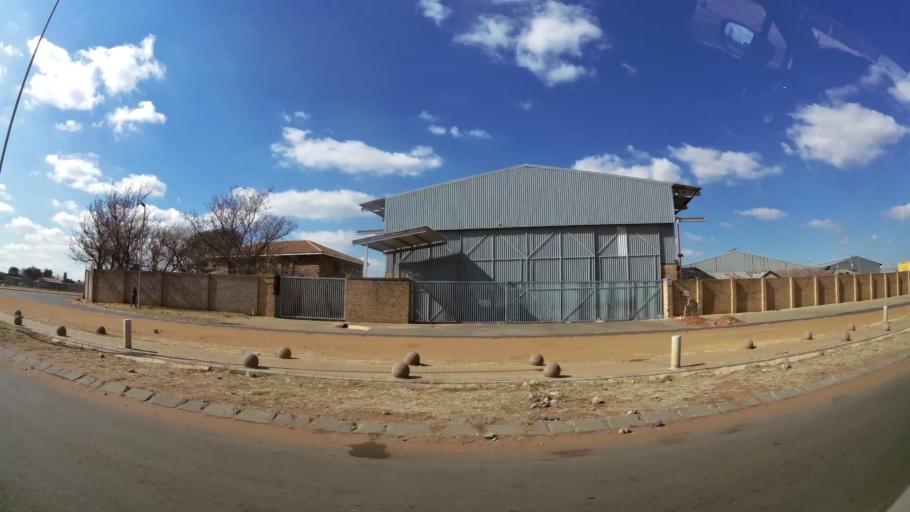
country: ZA
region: Gauteng
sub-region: West Rand District Municipality
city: Krugersdorp
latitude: -26.1439
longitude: 27.7918
